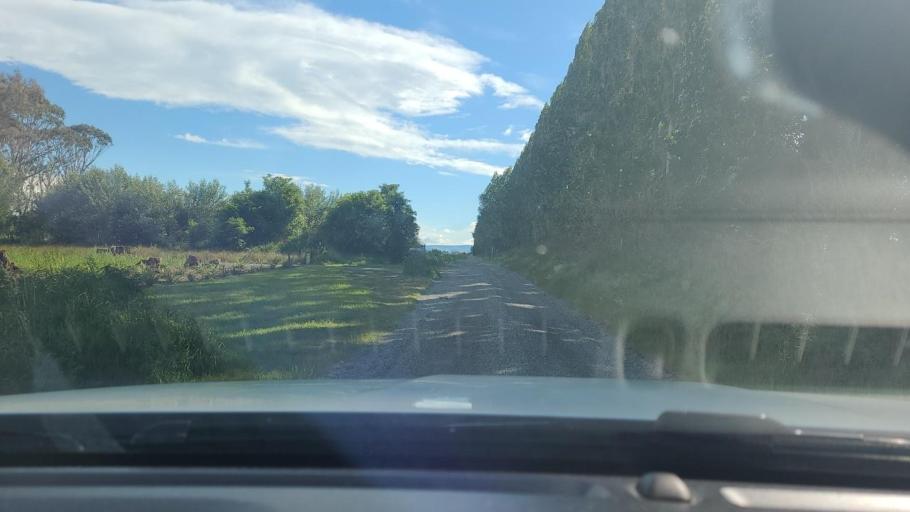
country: NZ
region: Southland
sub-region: Southland District
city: Winton
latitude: -46.1231
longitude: 168.2499
